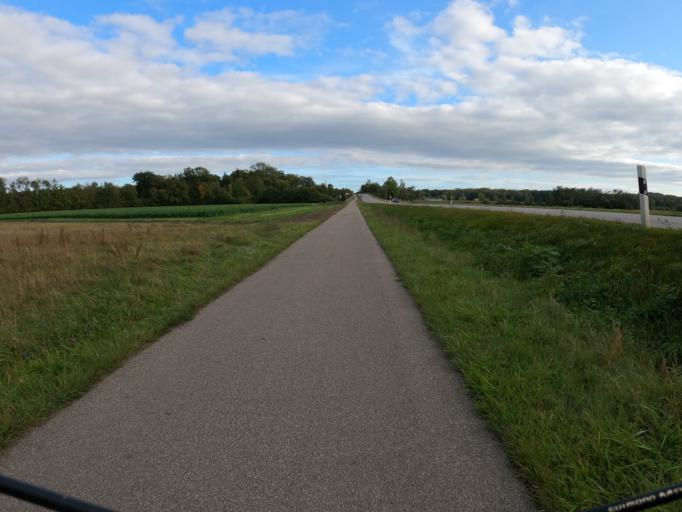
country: DE
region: Bavaria
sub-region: Swabia
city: Holzheim
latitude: 48.4045
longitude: 10.0870
